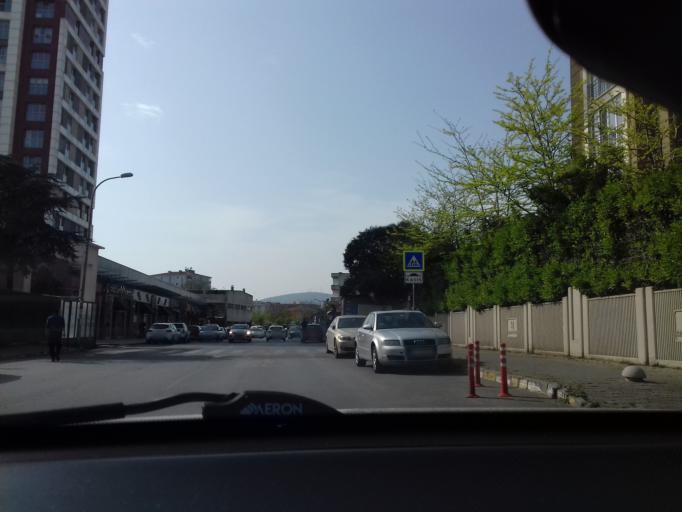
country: TR
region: Istanbul
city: Maltepe
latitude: 40.9135
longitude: 29.2094
